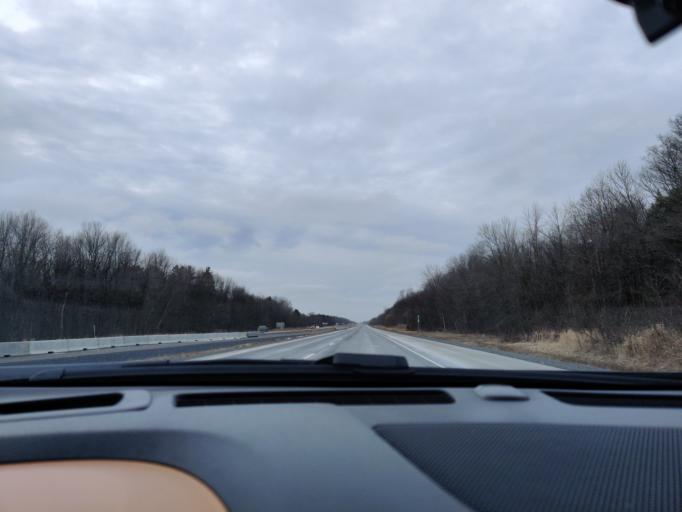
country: CA
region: Ontario
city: Cornwall
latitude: 45.1301
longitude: -74.5107
